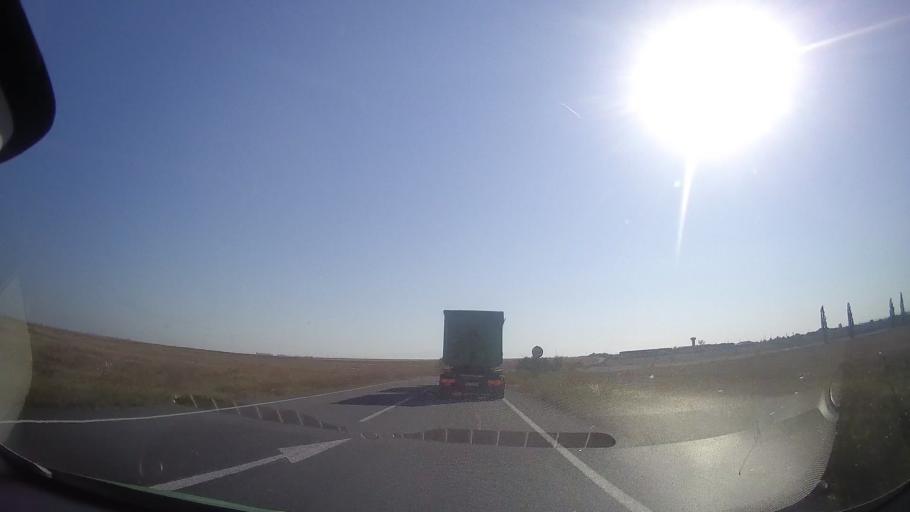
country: RO
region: Timis
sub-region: Comuna Ghizela
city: Ghizela
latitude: 45.7752
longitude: 21.6974
